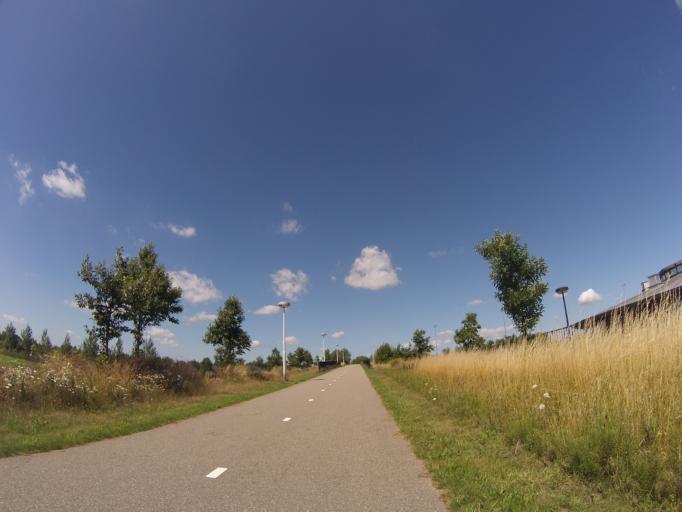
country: NL
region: Utrecht
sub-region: Stichtse Vecht
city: Spechtenkamp
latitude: 52.1101
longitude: 5.0291
